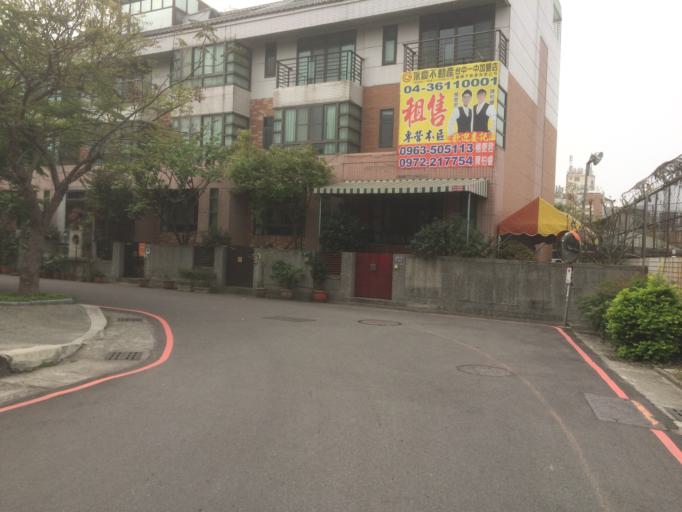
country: TW
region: Taiwan
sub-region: Taichung City
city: Taichung
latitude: 24.1803
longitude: 120.6991
